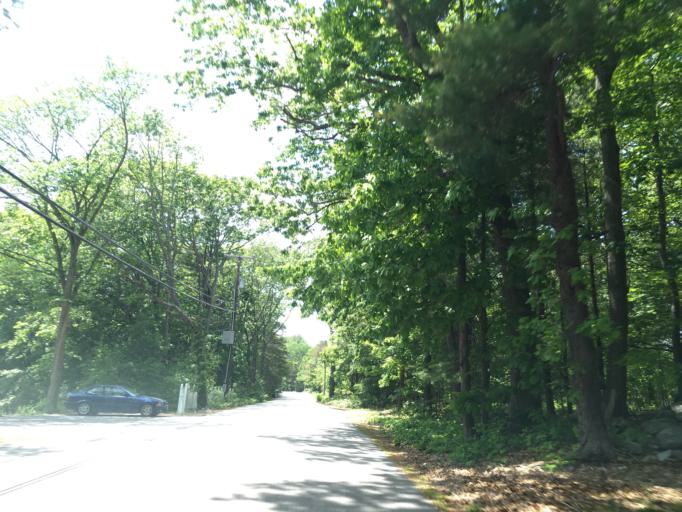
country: US
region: New Hampshire
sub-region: Rockingham County
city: Stratham Station
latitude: 43.0226
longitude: -70.8777
